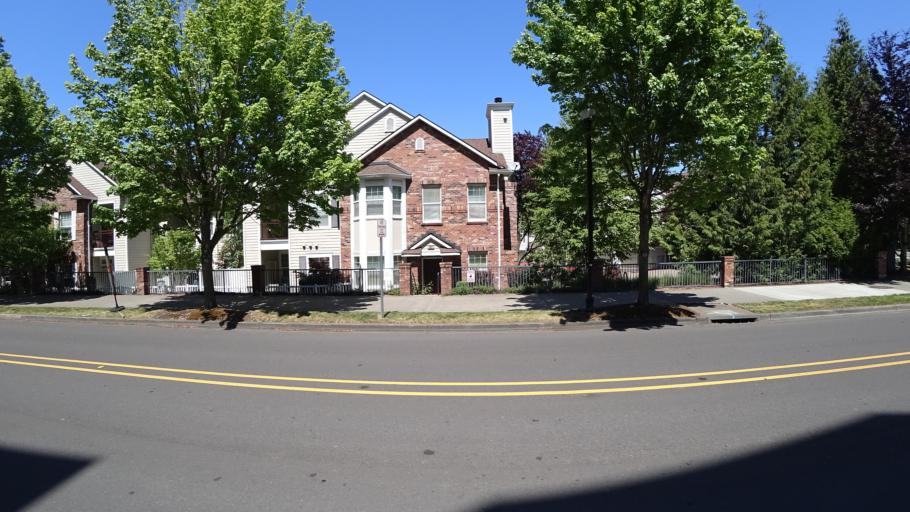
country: US
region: Oregon
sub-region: Washington County
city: Rockcreek
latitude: 45.5313
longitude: -122.9149
